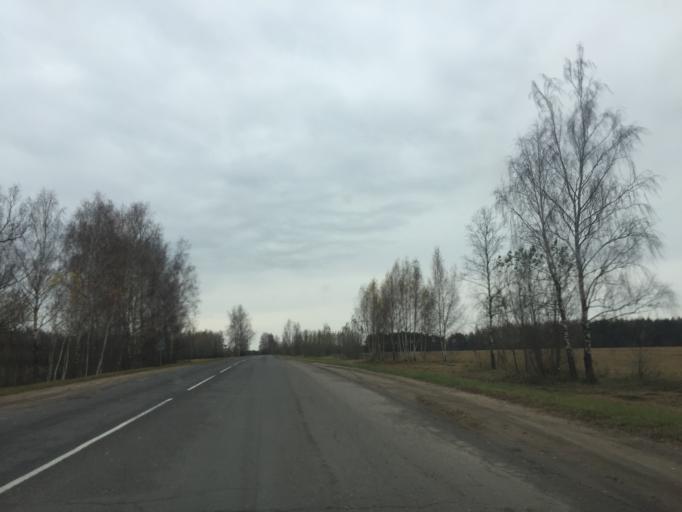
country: BY
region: Mogilev
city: Drybin
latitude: 54.1060
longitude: 31.0939
